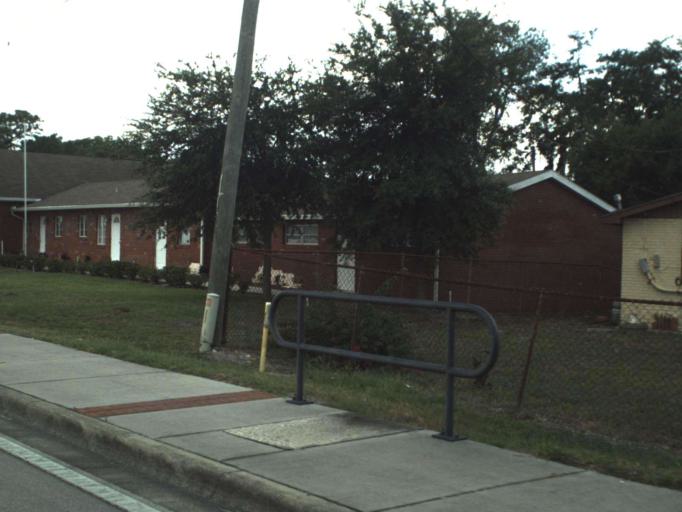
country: US
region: Florida
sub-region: Seminole County
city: Casselberry
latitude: 28.6776
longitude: -81.3364
